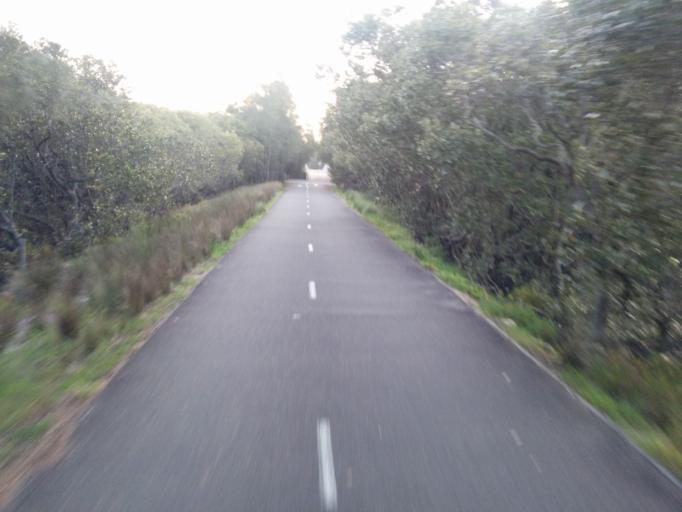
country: AU
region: New South Wales
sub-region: Canada Bay
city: Concord West
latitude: -33.8445
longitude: 151.0813
